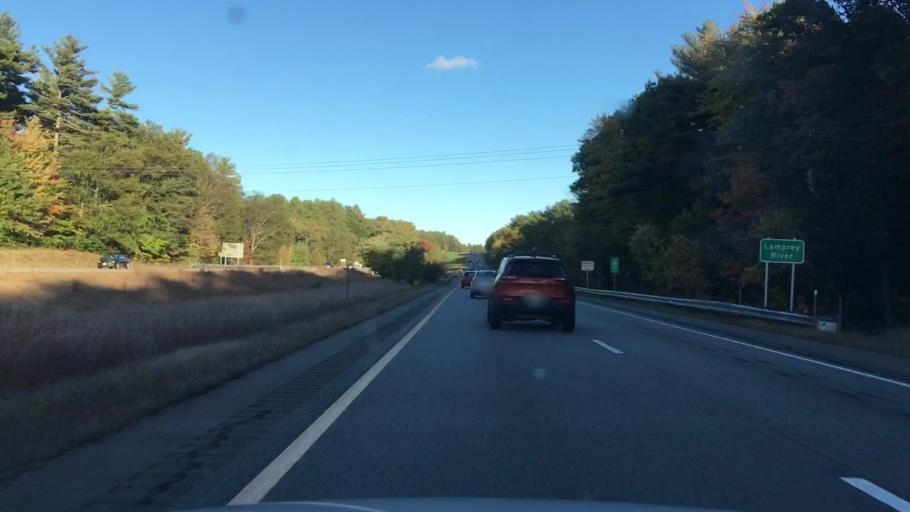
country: US
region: New Hampshire
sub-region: Rockingham County
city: Raymond
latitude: 43.0310
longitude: -71.1472
